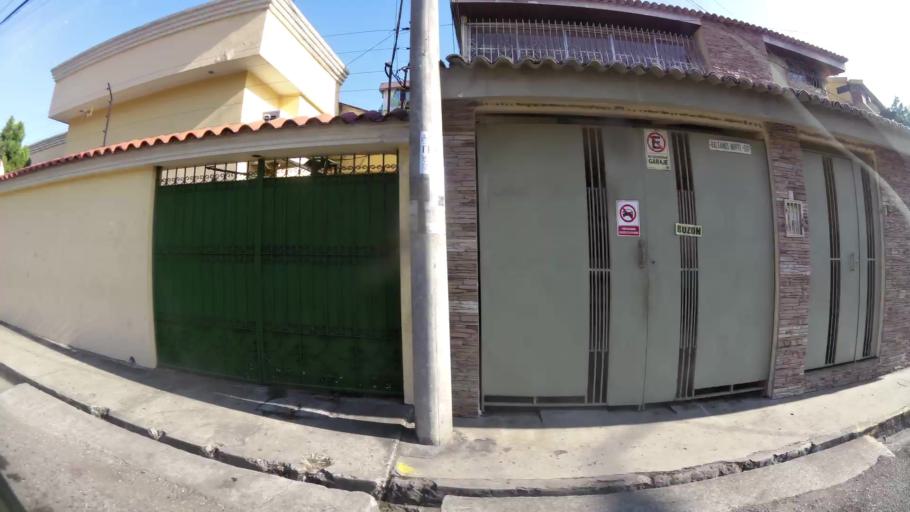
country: EC
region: Guayas
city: Guayaquil
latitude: -2.1669
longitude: -79.9025
